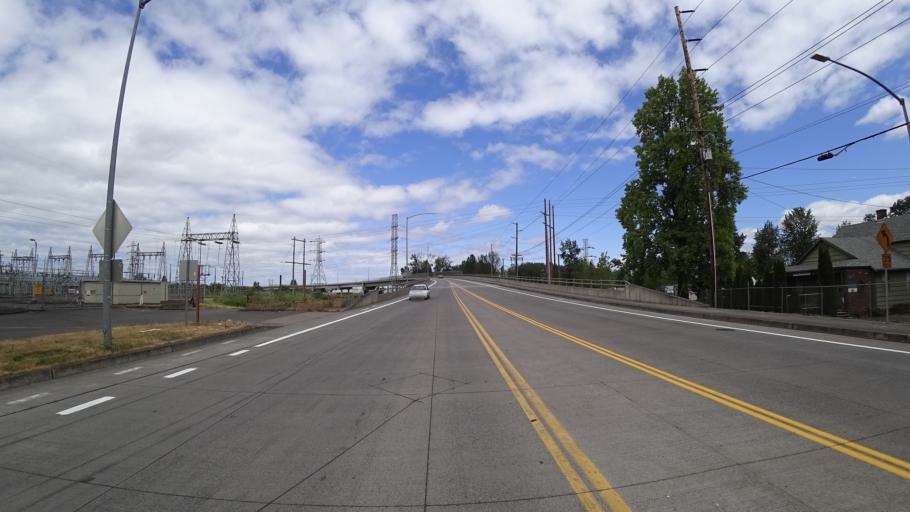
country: US
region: Oregon
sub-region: Washington County
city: West Haven
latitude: 45.6135
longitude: -122.7630
